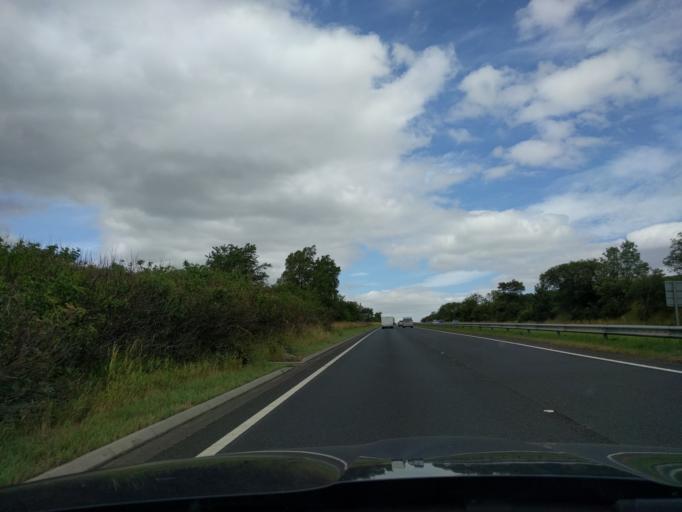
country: GB
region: England
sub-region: Northumberland
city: Alnwick
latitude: 55.3558
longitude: -1.7273
